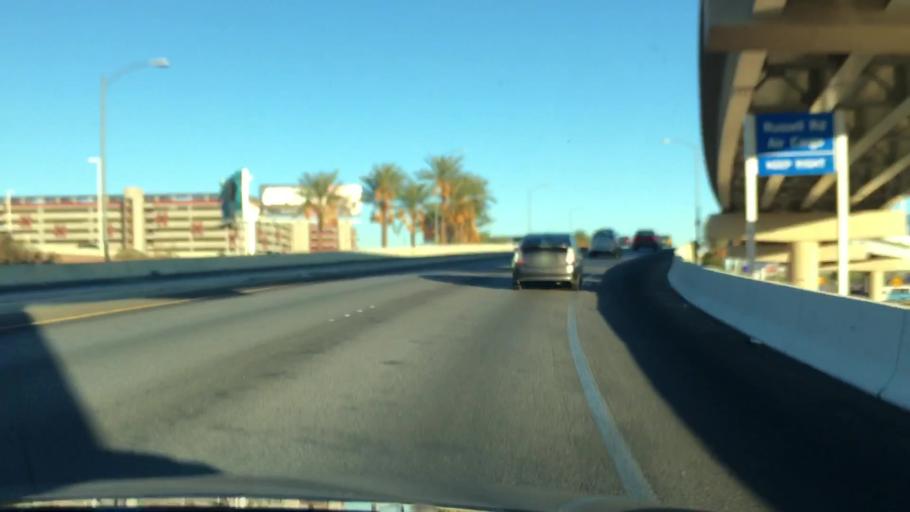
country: US
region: Nevada
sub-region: Clark County
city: Paradise
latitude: 36.0838
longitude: -115.1442
